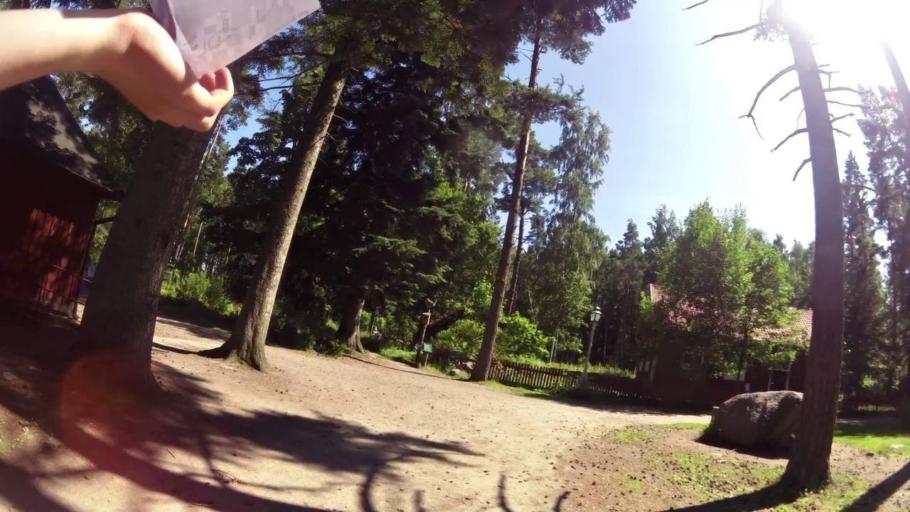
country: SE
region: OEstergoetland
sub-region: Linkopings Kommun
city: Linkoping
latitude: 58.4047
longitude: 15.5894
